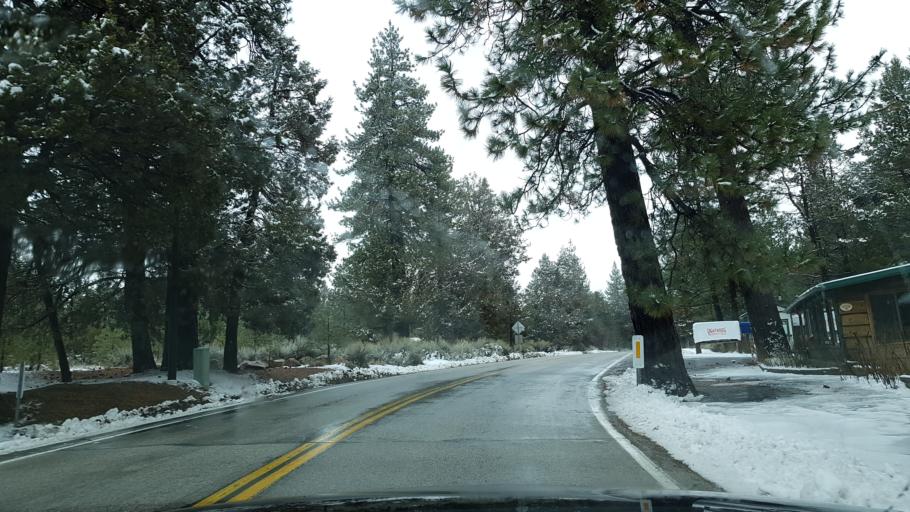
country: US
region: California
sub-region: San Bernardino County
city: Big Bear Lake
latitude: 34.2618
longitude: -116.9178
